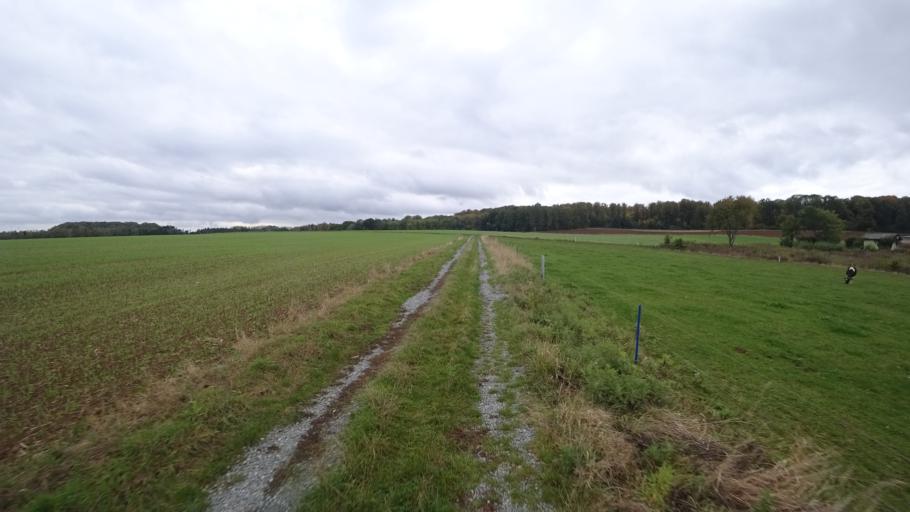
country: DE
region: Rheinland-Pfalz
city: Maxsain
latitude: 50.5466
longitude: 7.7699
